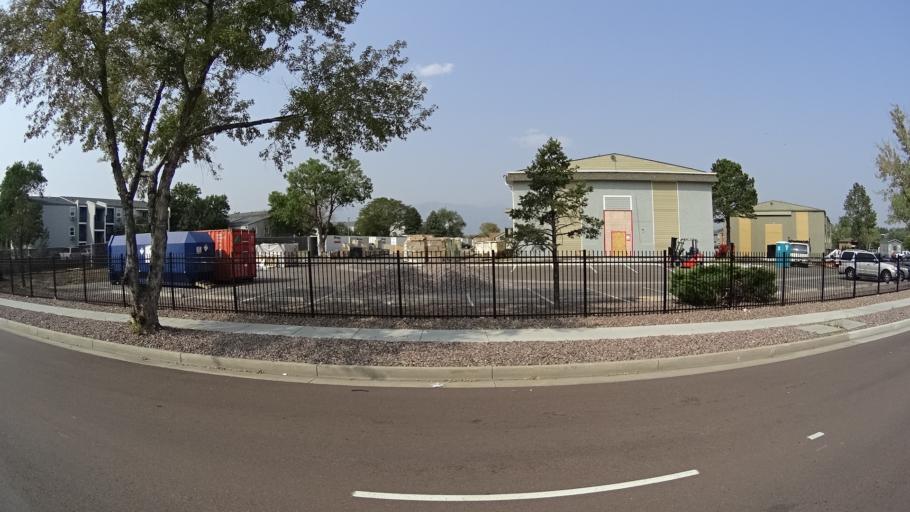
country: US
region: Colorado
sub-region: El Paso County
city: Stratmoor
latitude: 38.8169
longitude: -104.7665
